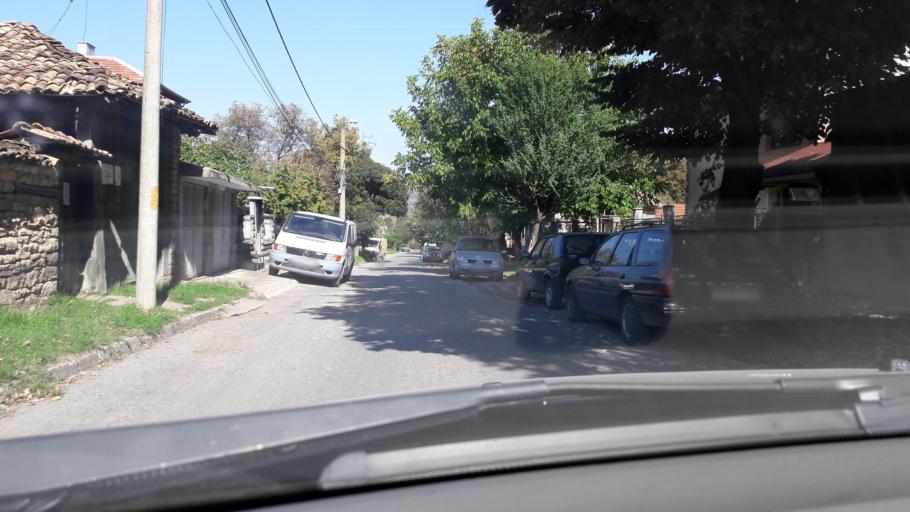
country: BG
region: Razgrad
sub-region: Obshtina Razgrad
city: Razgrad
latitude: 43.5226
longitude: 26.5129
